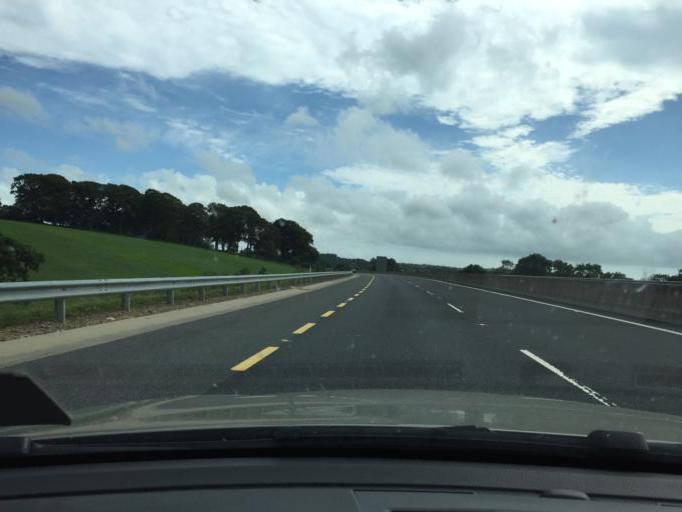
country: IE
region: Leinster
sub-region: Kilkenny
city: Mooncoin
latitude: 52.2501
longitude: -7.1909
